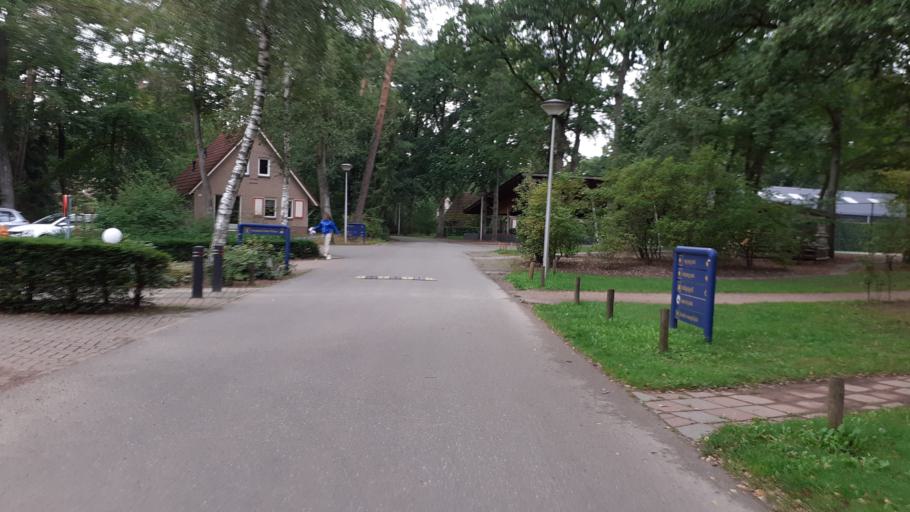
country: NL
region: Gelderland
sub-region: Gemeente Oldebroek
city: Oldebroek
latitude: 52.4394
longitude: 5.9547
